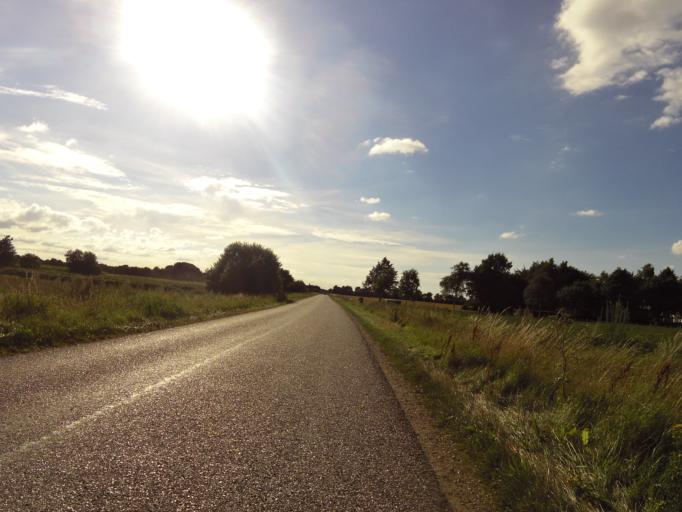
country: DK
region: South Denmark
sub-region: Haderslev Kommune
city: Vojens
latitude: 55.2062
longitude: 9.2707
